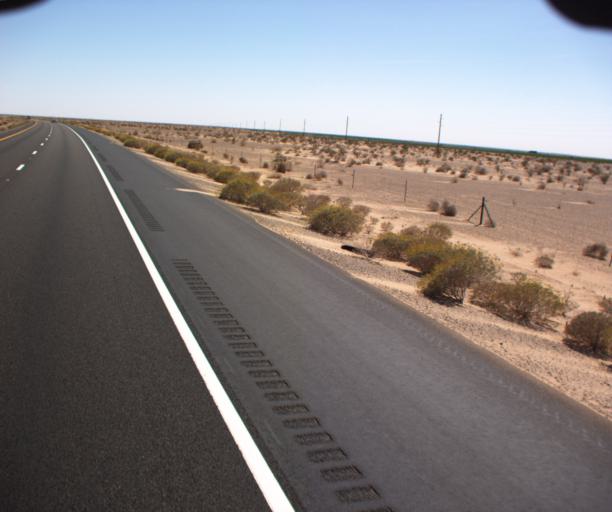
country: US
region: Arizona
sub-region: Yuma County
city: Somerton
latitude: 32.5160
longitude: -114.5615
